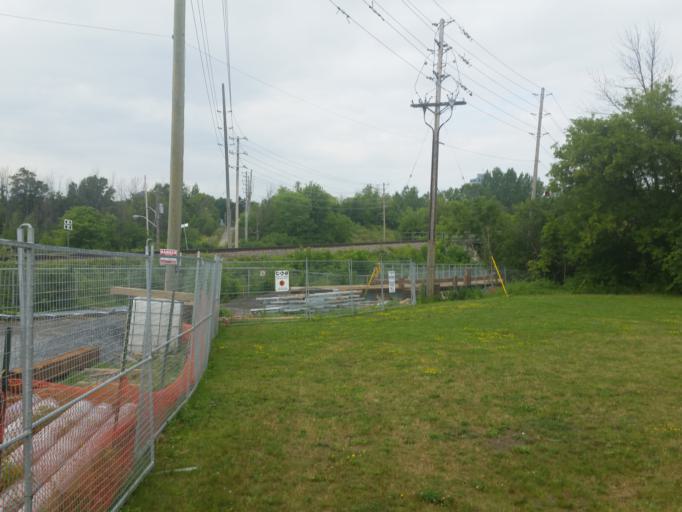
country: CA
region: Ontario
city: Ottawa
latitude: 45.3741
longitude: -75.6771
